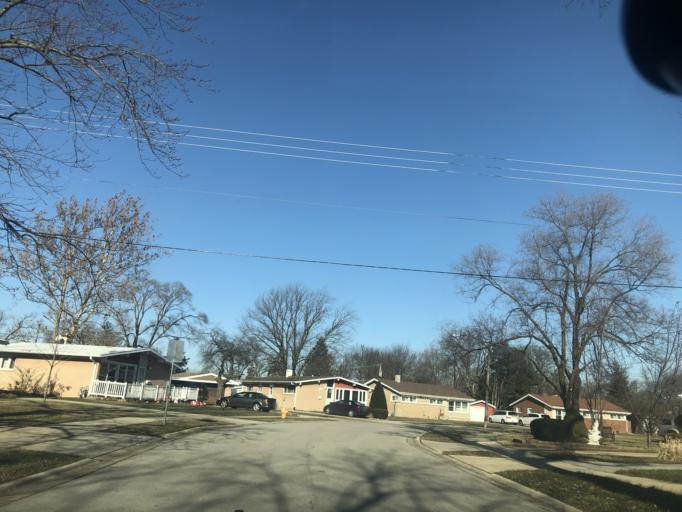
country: US
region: Illinois
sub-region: DuPage County
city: Addison
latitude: 41.9294
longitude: -87.9969
